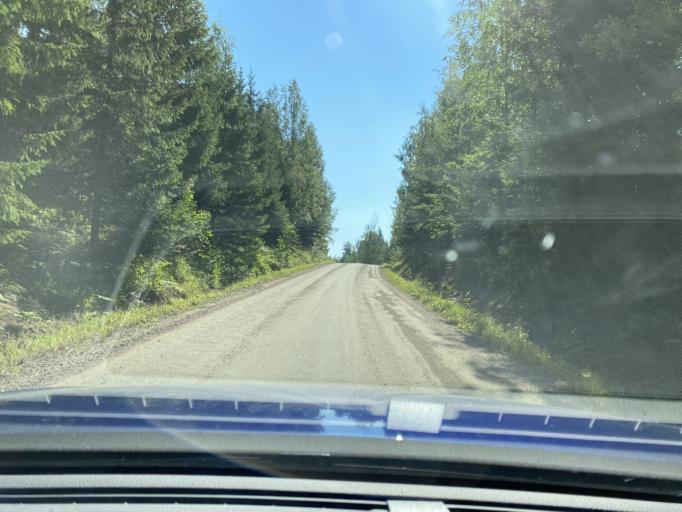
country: FI
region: Central Finland
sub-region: Jyvaeskylae
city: Korpilahti
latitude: 61.8722
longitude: 25.4171
